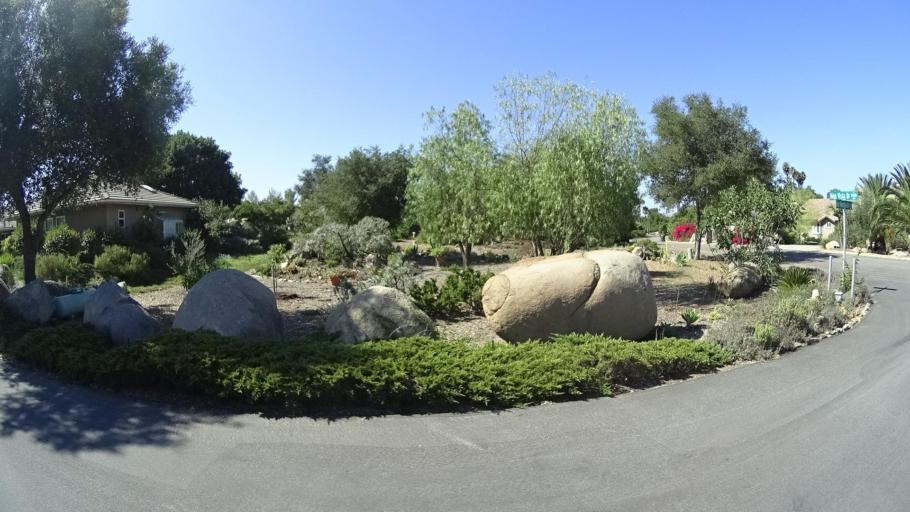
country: US
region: California
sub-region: San Diego County
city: Hidden Meadows
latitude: 33.2081
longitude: -117.1169
